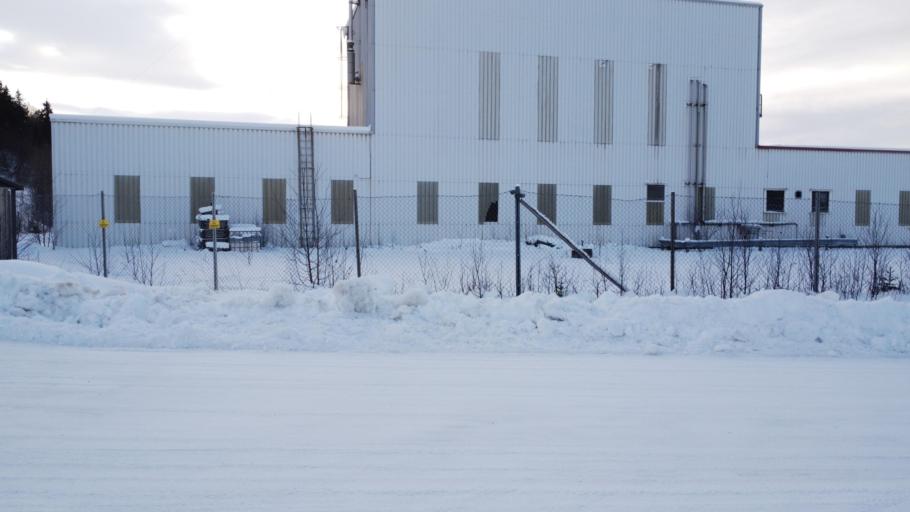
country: NO
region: Nordland
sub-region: Rana
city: Mo i Rana
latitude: 66.3246
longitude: 14.1527
